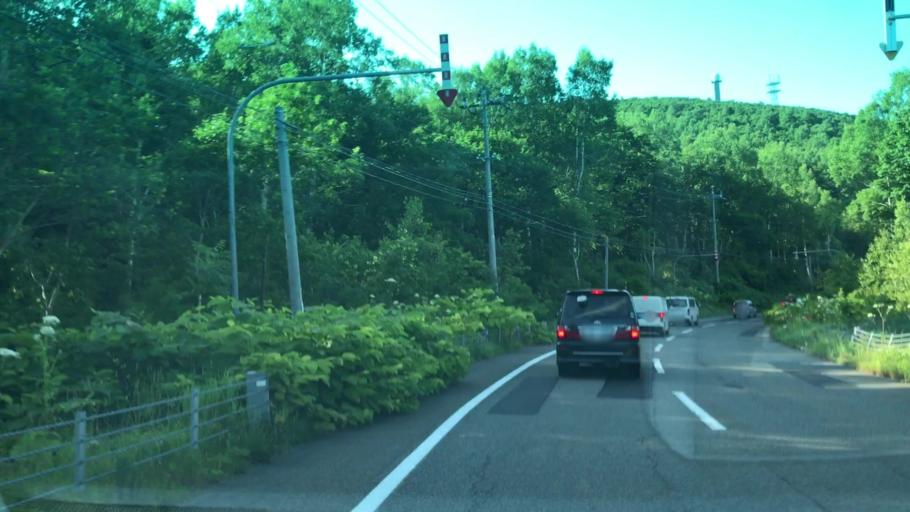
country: JP
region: Hokkaido
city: Otaru
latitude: 43.1319
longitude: 141.0116
